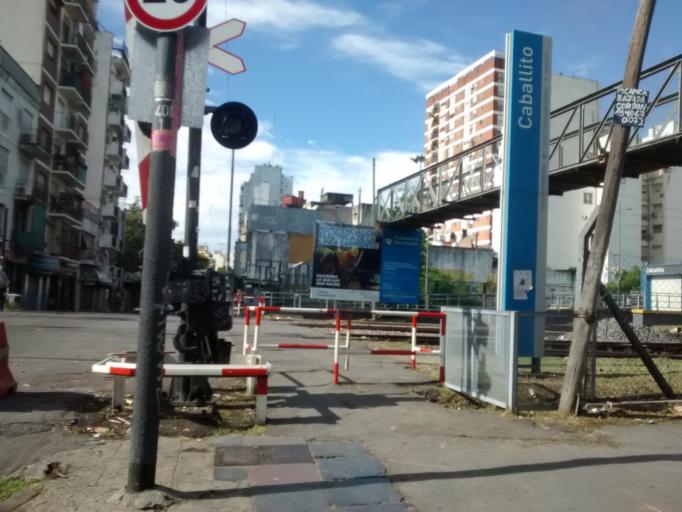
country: AR
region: Buenos Aires F.D.
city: Villa Santa Rita
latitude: -34.6185
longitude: -58.4424
